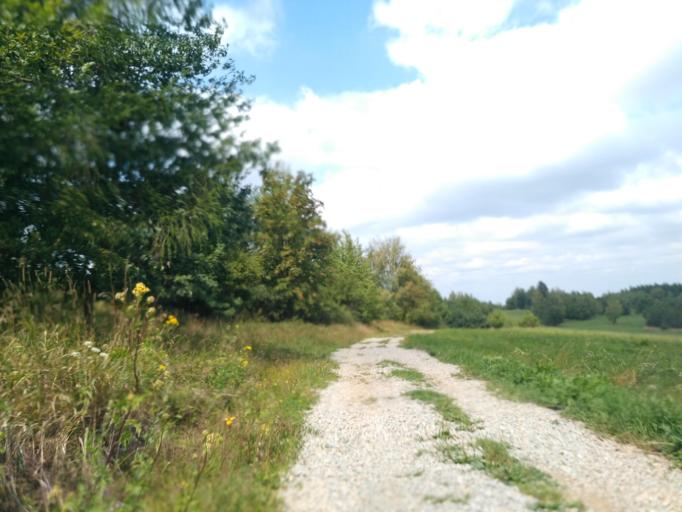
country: PL
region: Subcarpathian Voivodeship
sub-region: Powiat krosnienski
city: Iwonicz-Zdroj
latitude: 49.5734
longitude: 21.8095
